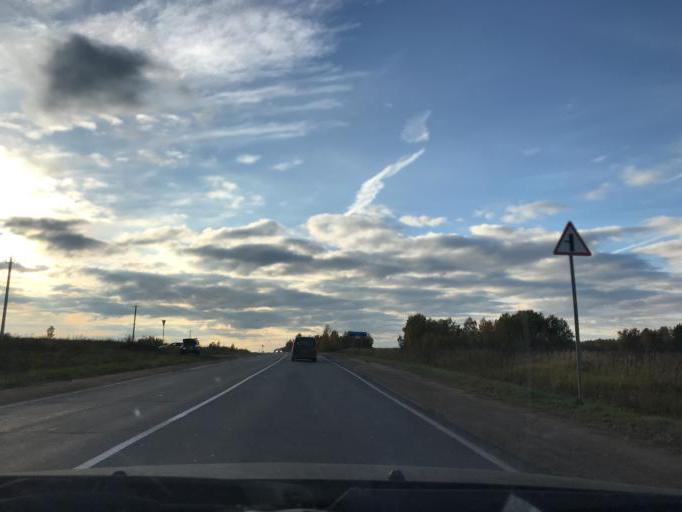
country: RU
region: Kaluga
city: Kurovskoye
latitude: 54.5292
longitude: 35.9681
